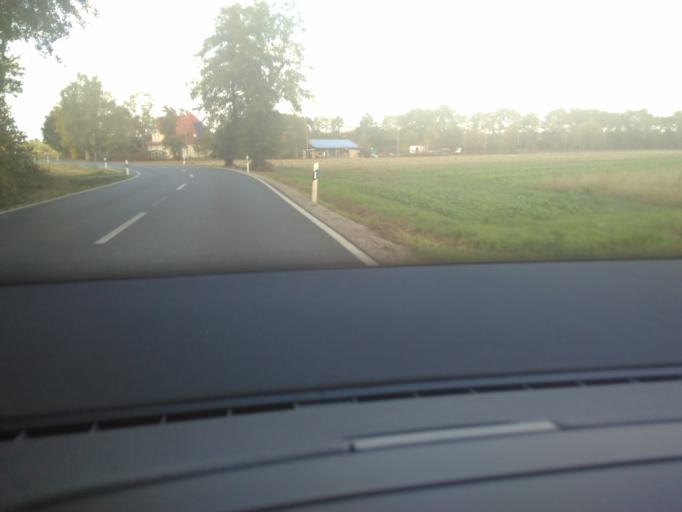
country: DE
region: North Rhine-Westphalia
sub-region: Regierungsbezirk Detmold
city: Verl
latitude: 51.9063
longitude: 8.5184
